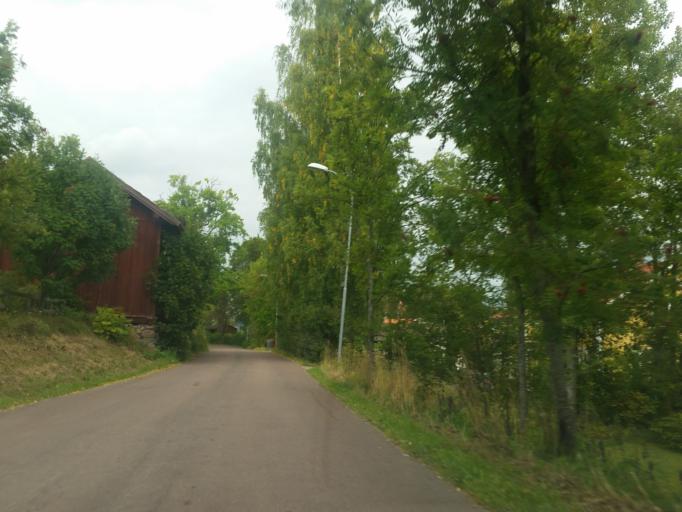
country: SE
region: Dalarna
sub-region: Leksand Municipality
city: Smedby
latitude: 60.6774
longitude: 15.1037
